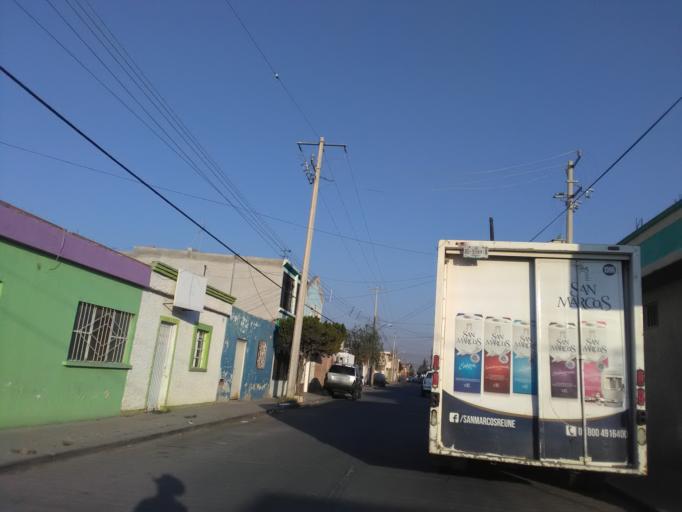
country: MX
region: Durango
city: Victoria de Durango
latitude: 24.0383
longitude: -104.6396
